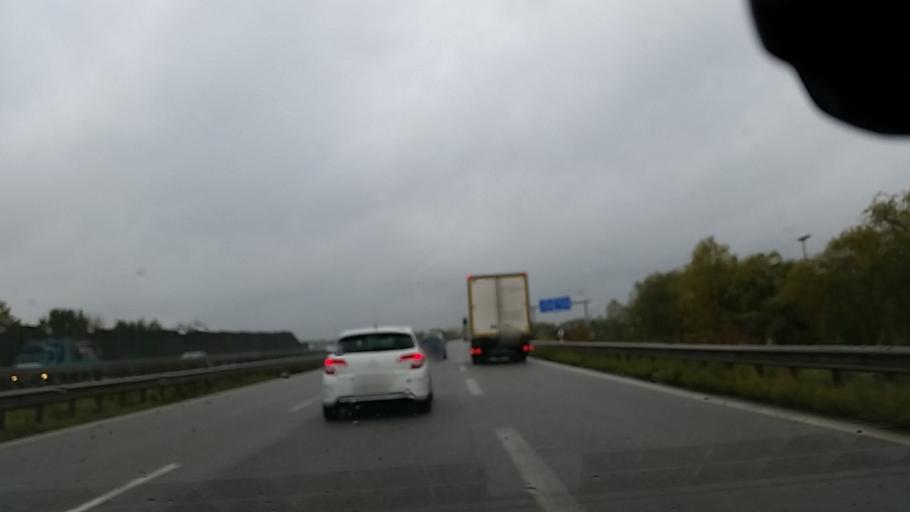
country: DE
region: Hamburg
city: Rothenburgsort
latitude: 53.5041
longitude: 10.0833
